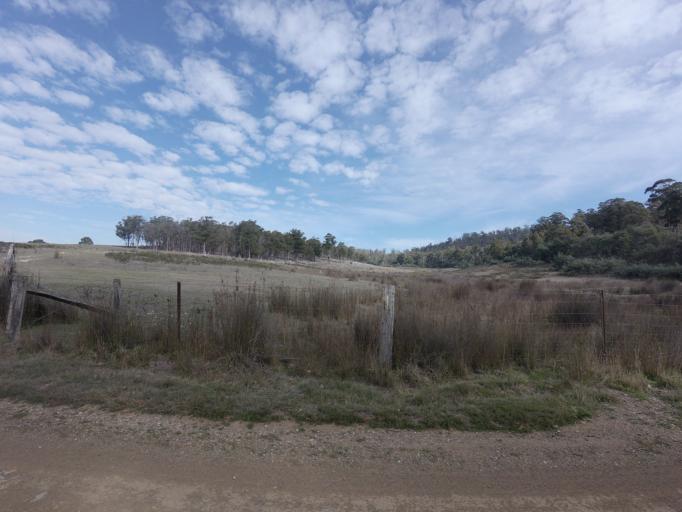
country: AU
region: Tasmania
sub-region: Sorell
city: Sorell
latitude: -42.5670
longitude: 147.4766
